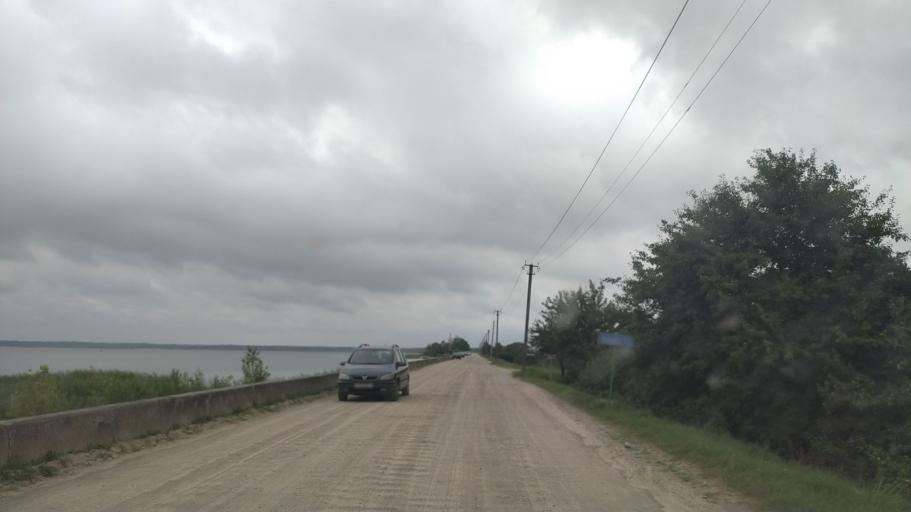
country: BY
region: Brest
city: Byaroza
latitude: 52.6030
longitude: 24.8778
